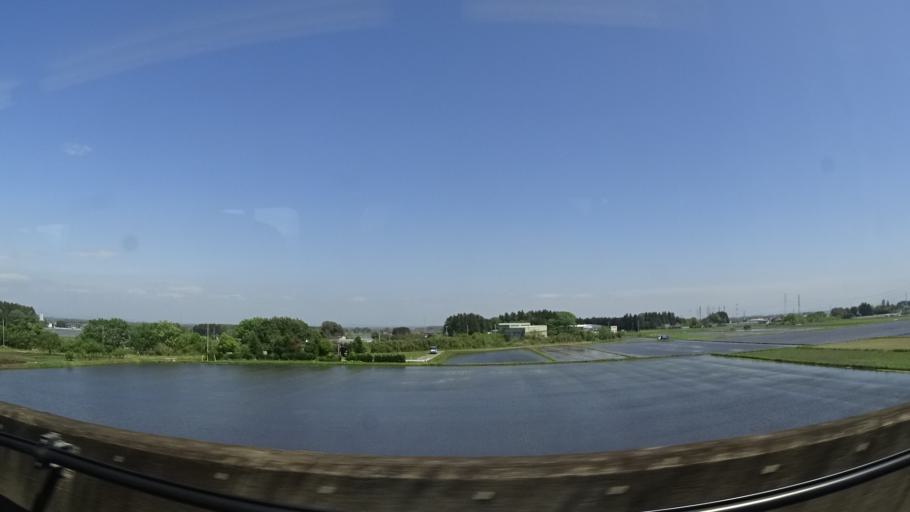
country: JP
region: Tochigi
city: Ujiie
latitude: 36.6698
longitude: 139.9152
